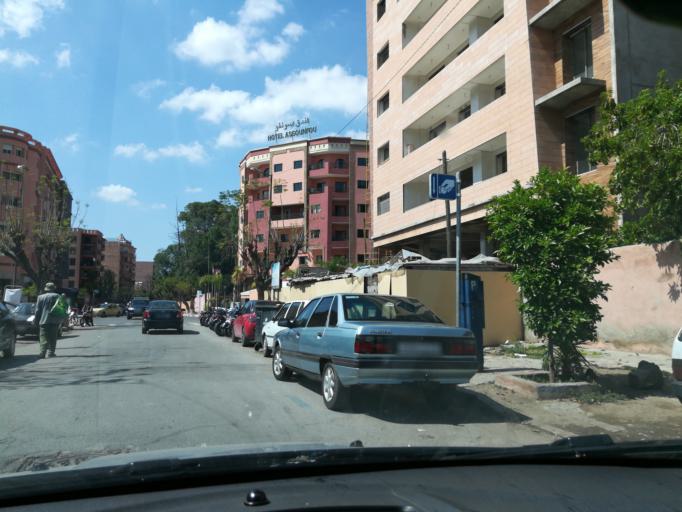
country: MA
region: Marrakech-Tensift-Al Haouz
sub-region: Marrakech
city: Marrakesh
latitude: 31.6340
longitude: -8.0065
